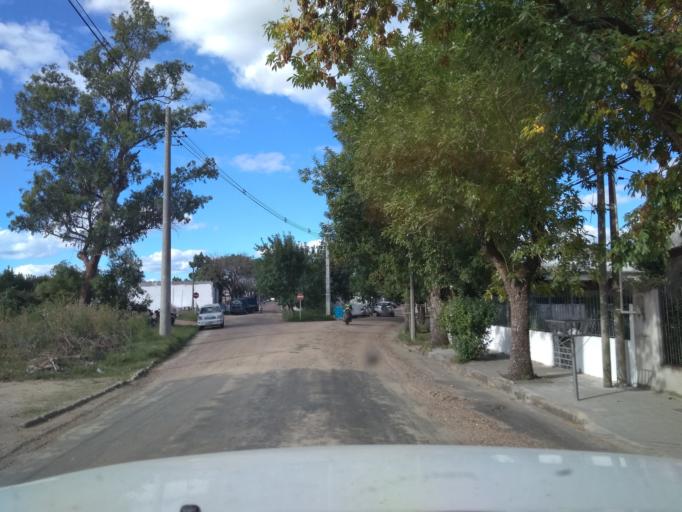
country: UY
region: Florida
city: Florida
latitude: -34.0940
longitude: -56.2225
